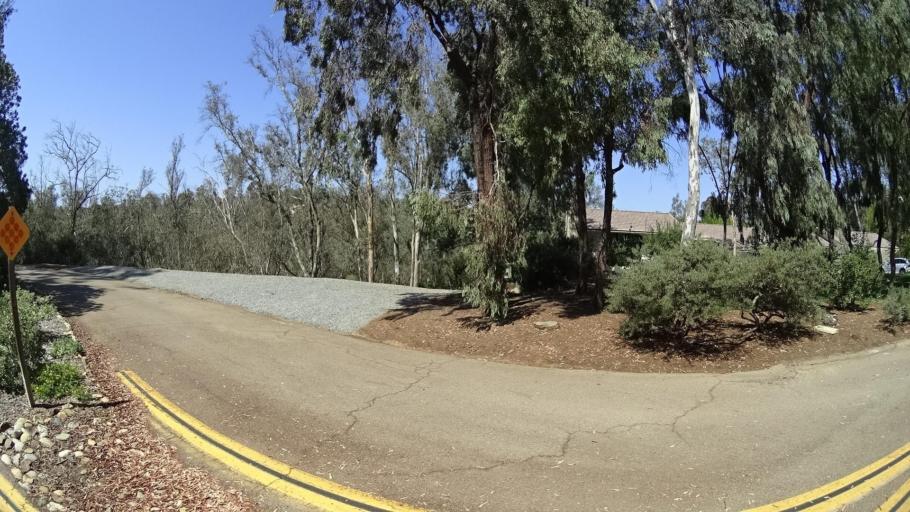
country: US
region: California
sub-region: San Diego County
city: Rancho Santa Fe
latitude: 32.9945
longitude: -117.2229
